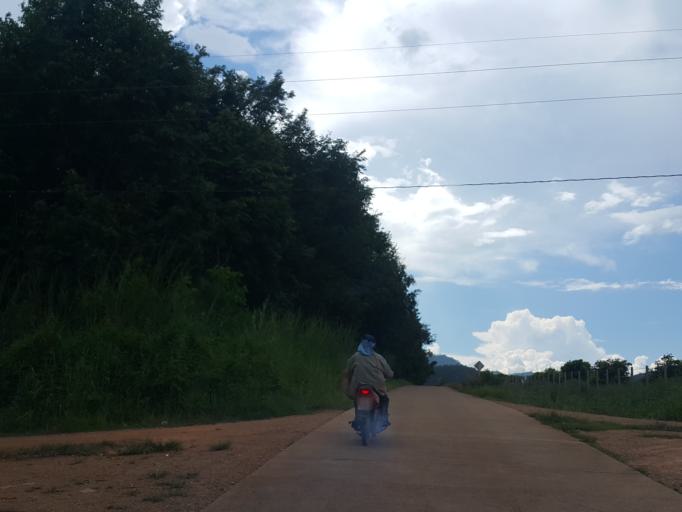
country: TH
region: Chiang Mai
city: Phrao
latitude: 19.3337
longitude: 99.1587
